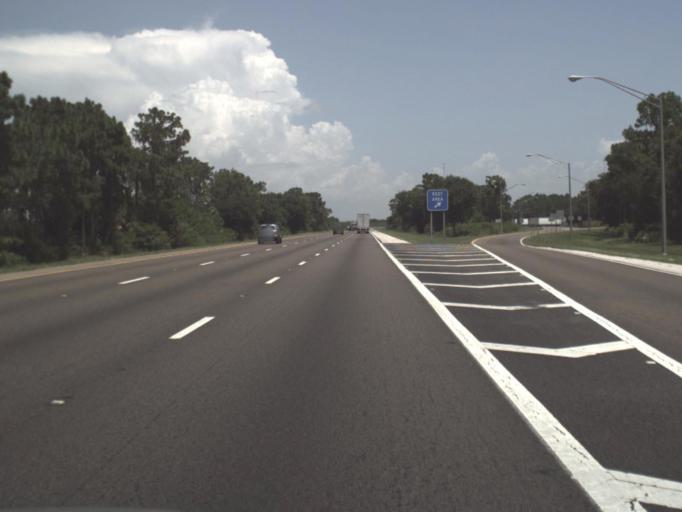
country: US
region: Florida
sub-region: Hillsborough County
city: Ruskin
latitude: 27.6794
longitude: -82.4245
